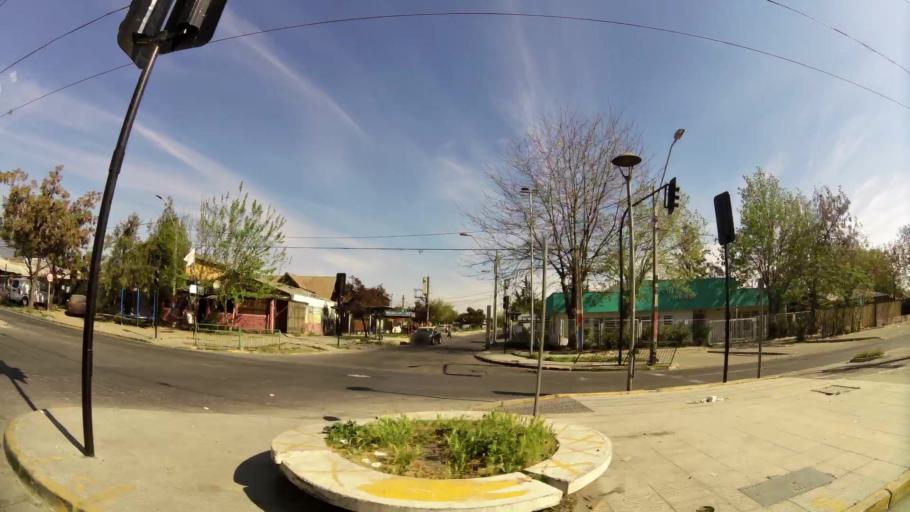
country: CL
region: Santiago Metropolitan
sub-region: Provincia de Santiago
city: Villa Presidente Frei, Nunoa, Santiago, Chile
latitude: -33.4765
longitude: -70.5720
